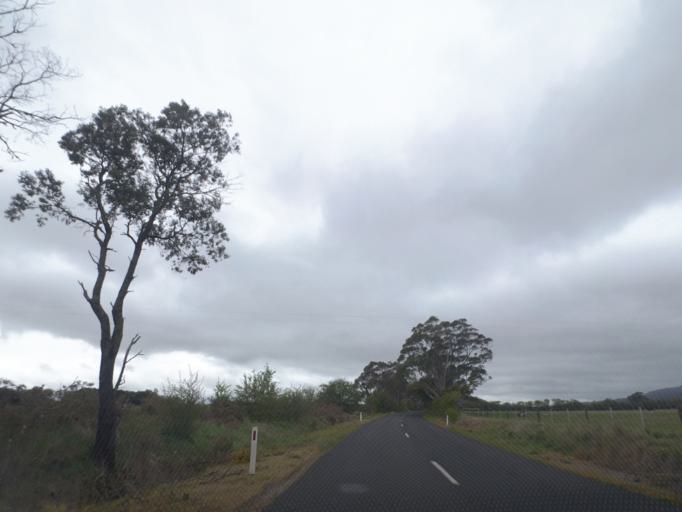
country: AU
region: Victoria
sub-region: Hume
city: Sunbury
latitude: -37.3239
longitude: 144.5630
